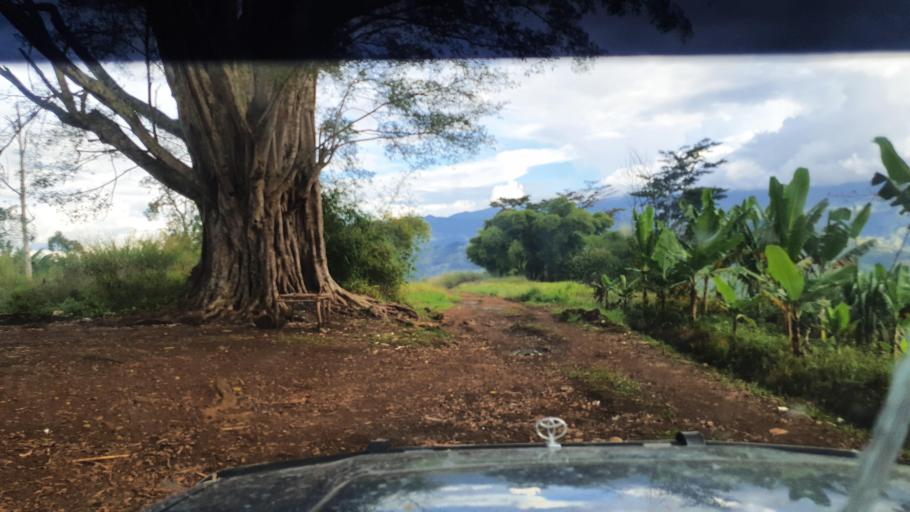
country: PG
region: Jiwaka
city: Minj
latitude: -5.9291
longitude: 144.8196
